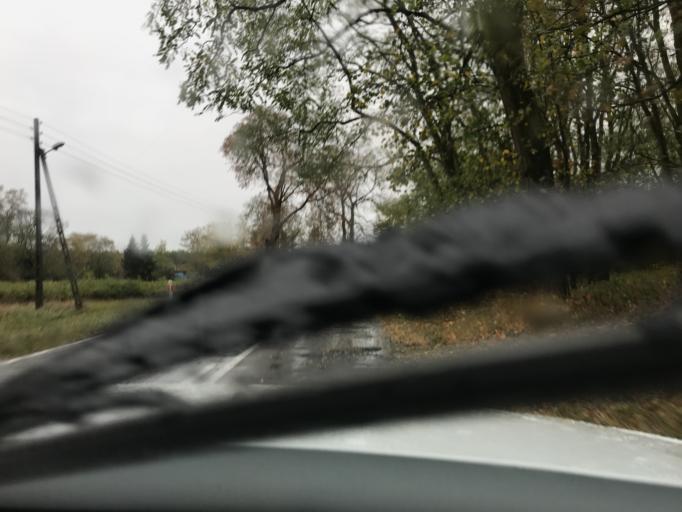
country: DE
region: Brandenburg
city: Neulewin
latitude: 52.7676
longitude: 14.3200
